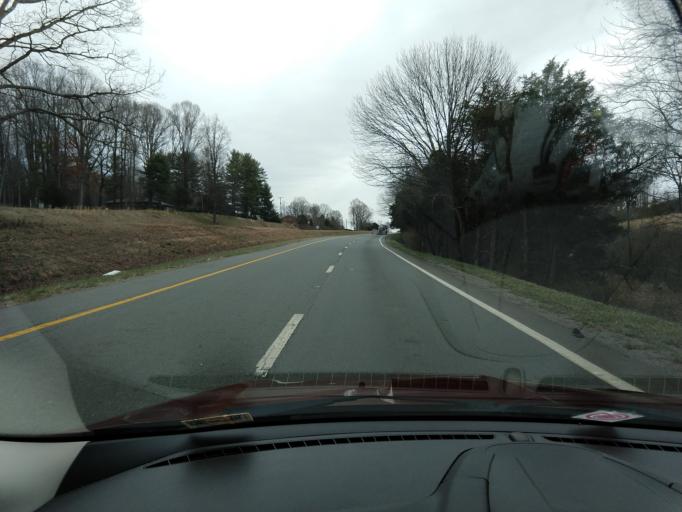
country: US
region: Virginia
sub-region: Henry County
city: Stanleytown
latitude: 36.8413
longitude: -79.9156
